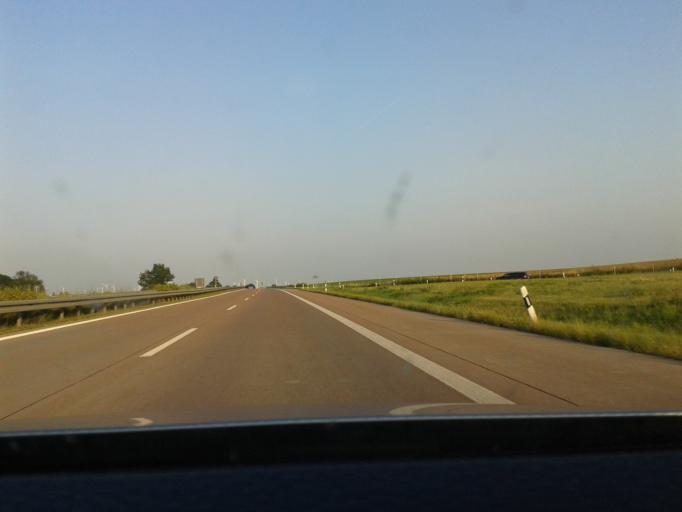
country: DE
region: Saxony
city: Mutzschen
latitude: 51.2421
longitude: 12.8600
